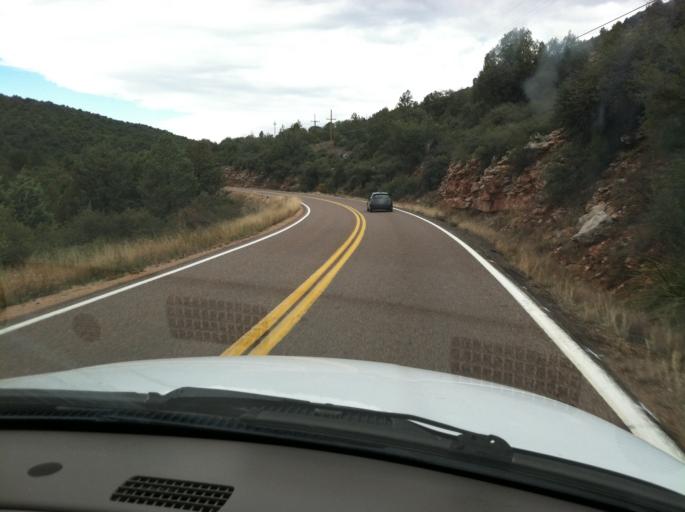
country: US
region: Arizona
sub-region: Gila County
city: Payson
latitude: 34.3175
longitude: -111.3747
